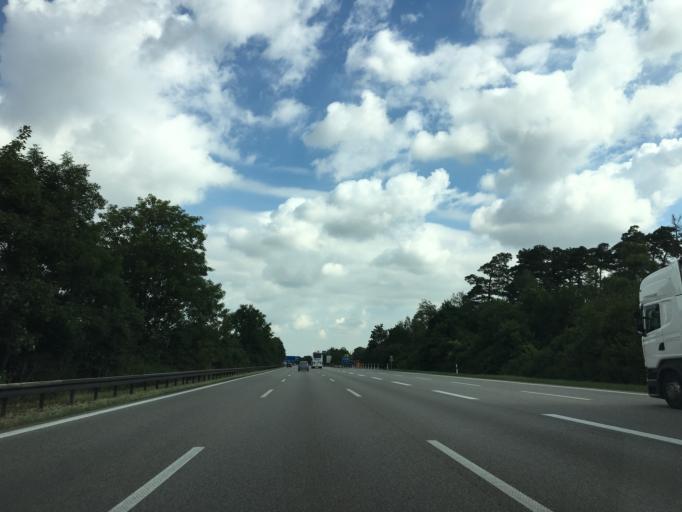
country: DE
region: Bavaria
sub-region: Upper Bavaria
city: Vaterstetten
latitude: 48.1202
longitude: 11.7583
